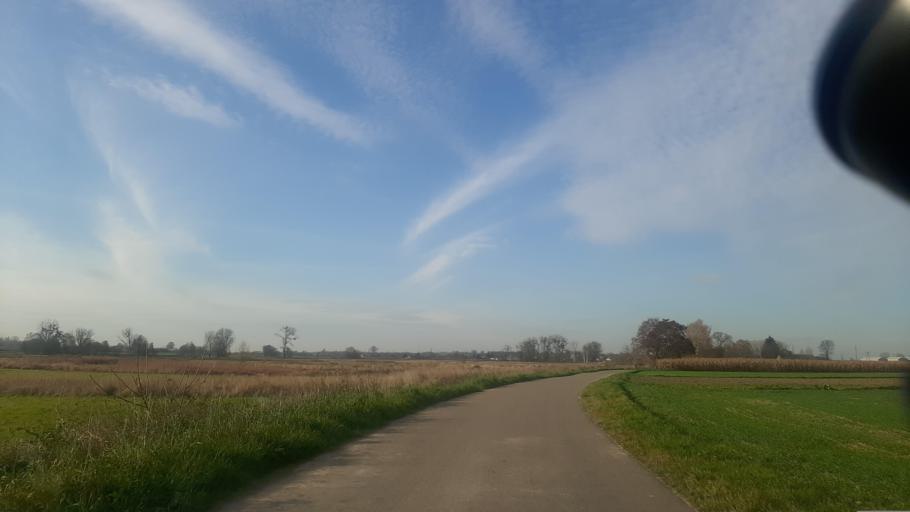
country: PL
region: Lublin Voivodeship
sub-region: Powiat pulawski
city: Markuszow
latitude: 51.3634
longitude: 22.2775
